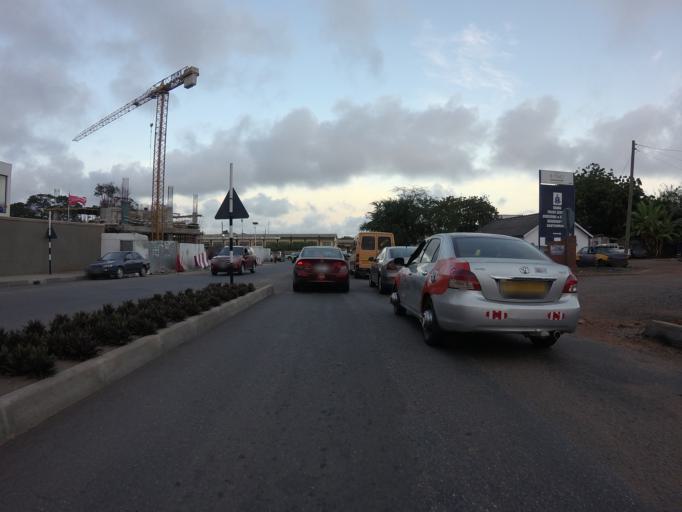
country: GH
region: Greater Accra
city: Accra
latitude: 5.5728
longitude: -0.1806
